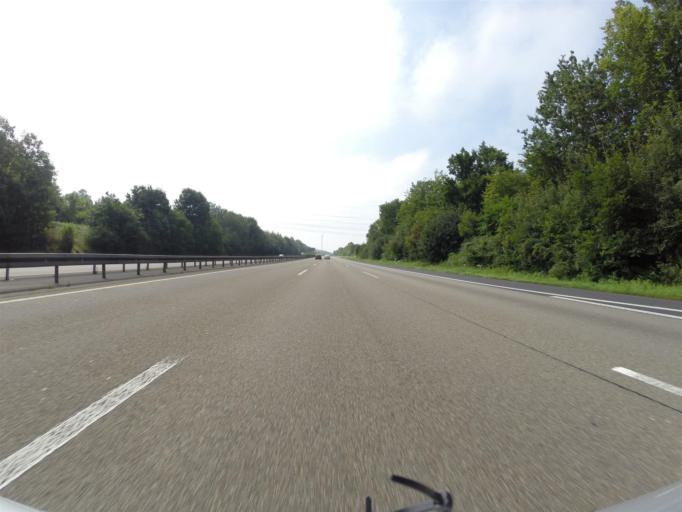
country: DE
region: Hesse
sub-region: Regierungsbezirk Kassel
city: Lohfelden
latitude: 51.2608
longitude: 9.5168
